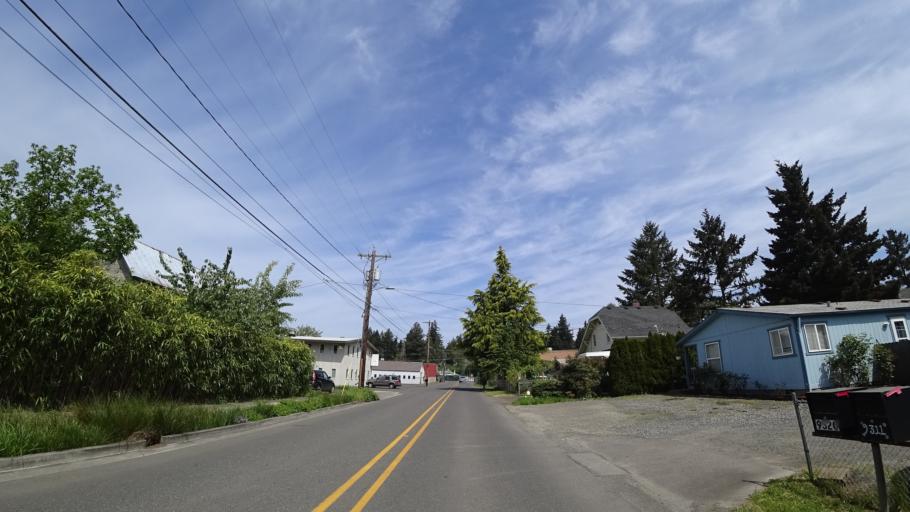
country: US
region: Oregon
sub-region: Clackamas County
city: Milwaukie
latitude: 45.4562
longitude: -122.6046
